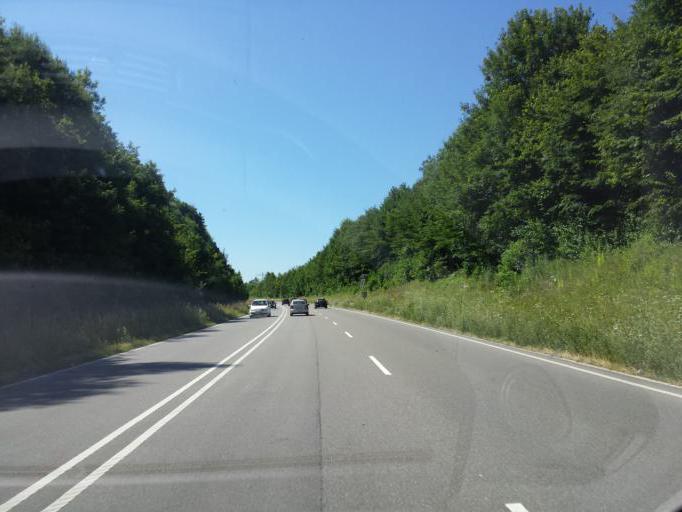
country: DE
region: Baden-Wuerttemberg
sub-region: Tuebingen Region
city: Sipplingen
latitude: 47.8124
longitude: 9.1145
